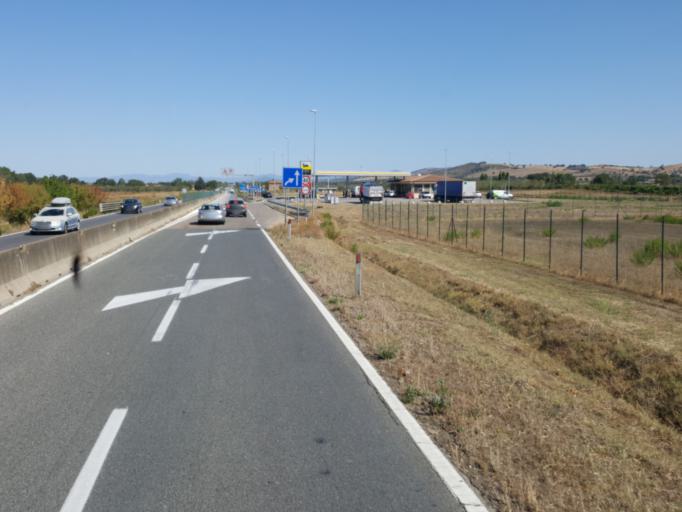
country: IT
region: Tuscany
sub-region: Provincia di Grosseto
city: Grosseto
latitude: 42.6734
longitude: 11.1416
